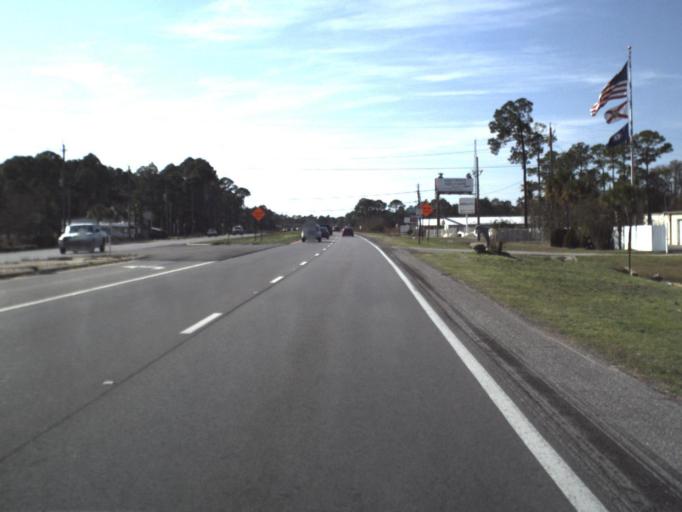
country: US
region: Florida
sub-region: Bay County
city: Panama City Beach
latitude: 30.1890
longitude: -85.7772
